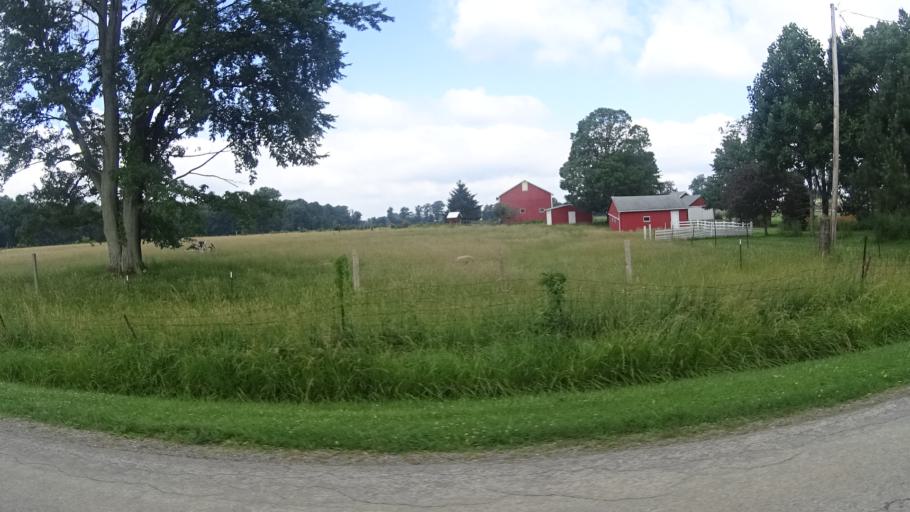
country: US
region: Ohio
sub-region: Huron County
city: Wakeman
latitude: 41.3003
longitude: -82.4429
